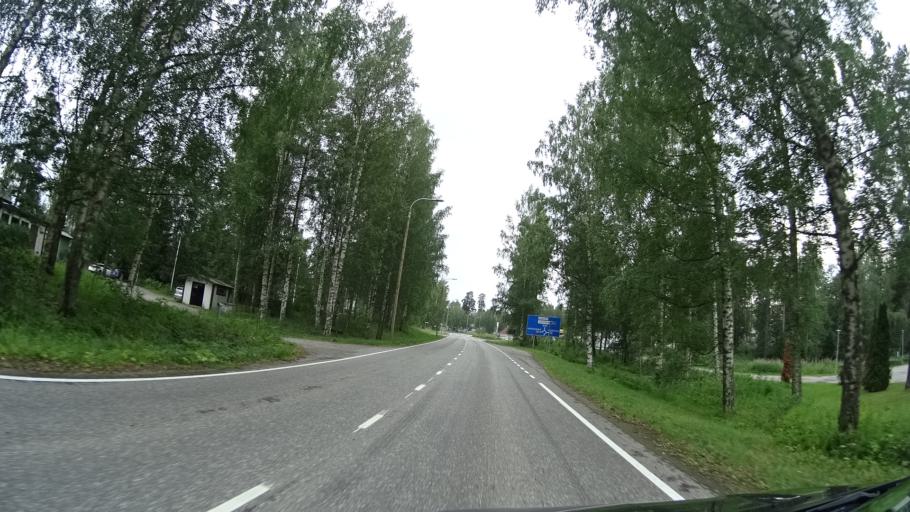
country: FI
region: Southern Savonia
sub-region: Savonlinna
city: Punkaharju
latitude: 61.7573
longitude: 29.3968
